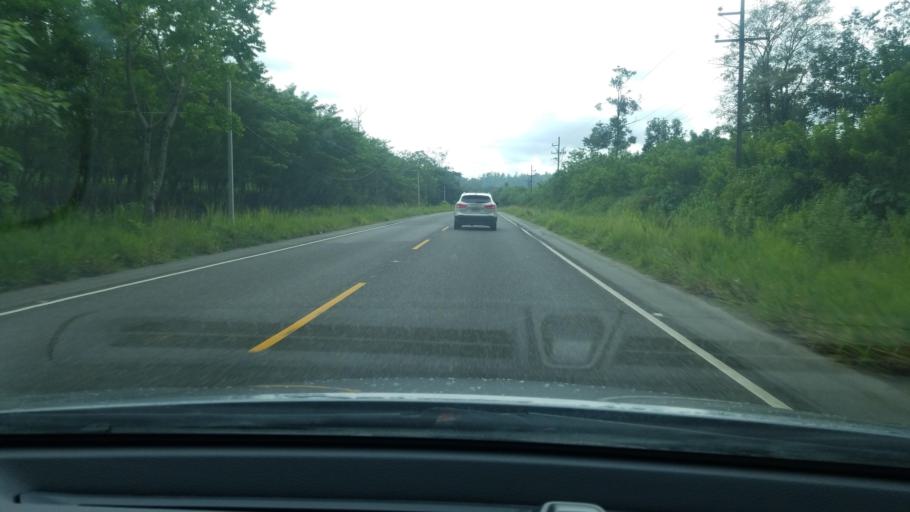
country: HN
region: Cortes
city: Potrerillos
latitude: 15.6153
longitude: -88.2769
